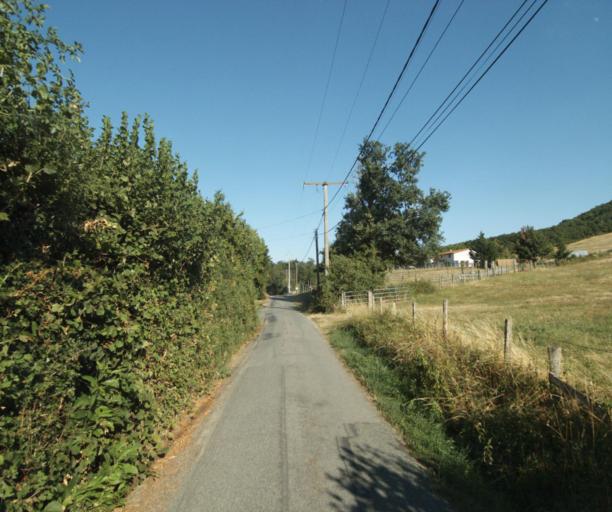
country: FR
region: Rhone-Alpes
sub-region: Departement du Rhone
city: Lentilly
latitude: 45.7990
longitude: 4.6599
